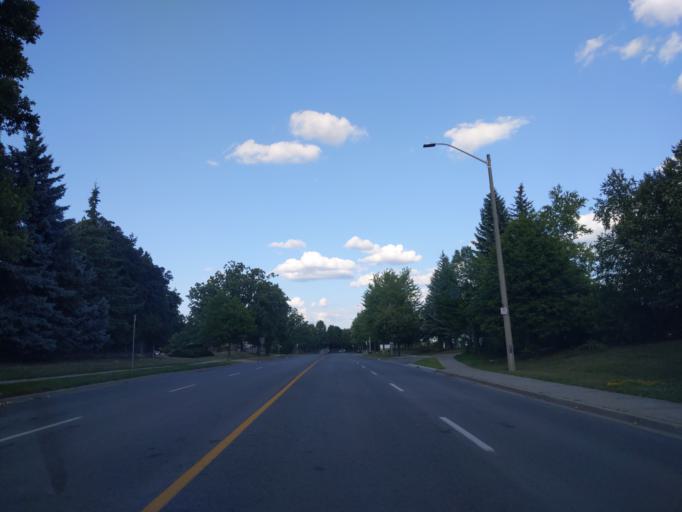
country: CA
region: Ontario
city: Markham
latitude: 43.8599
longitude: -79.3461
